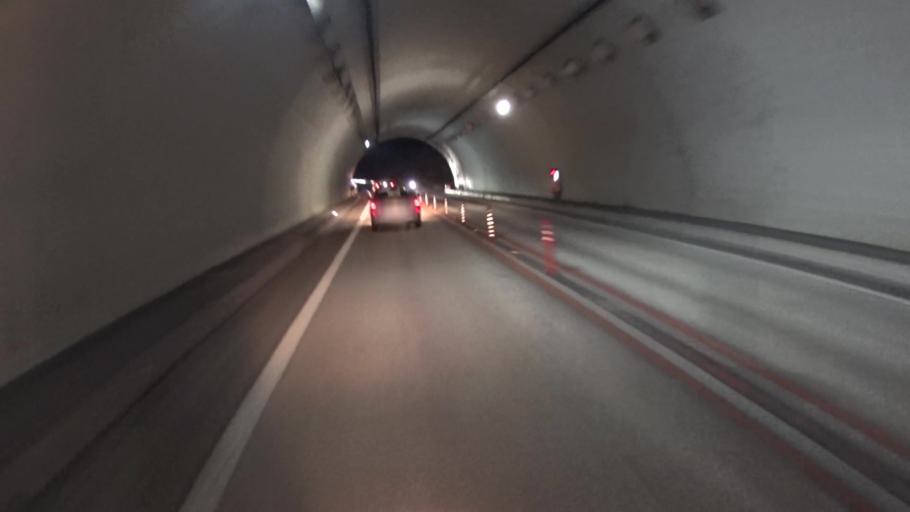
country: JP
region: Kyoto
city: Ayabe
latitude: 35.3163
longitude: 135.3195
